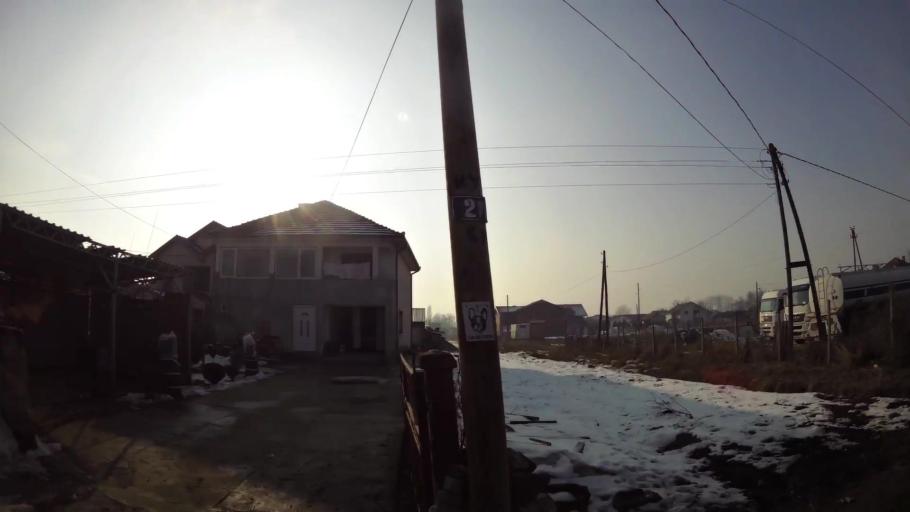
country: MK
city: Kadino
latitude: 41.9635
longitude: 21.5982
